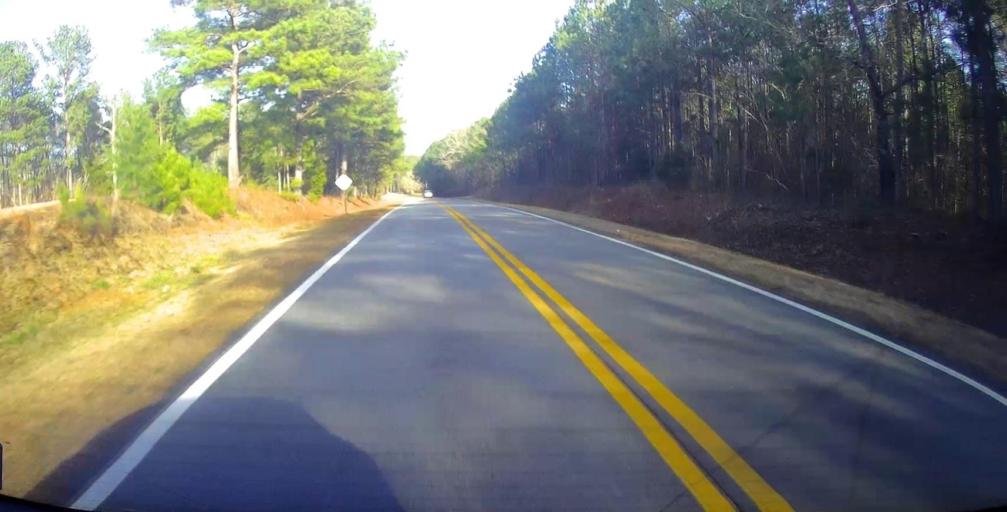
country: US
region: Georgia
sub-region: Bibb County
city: West Point
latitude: 32.8347
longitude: -83.9259
